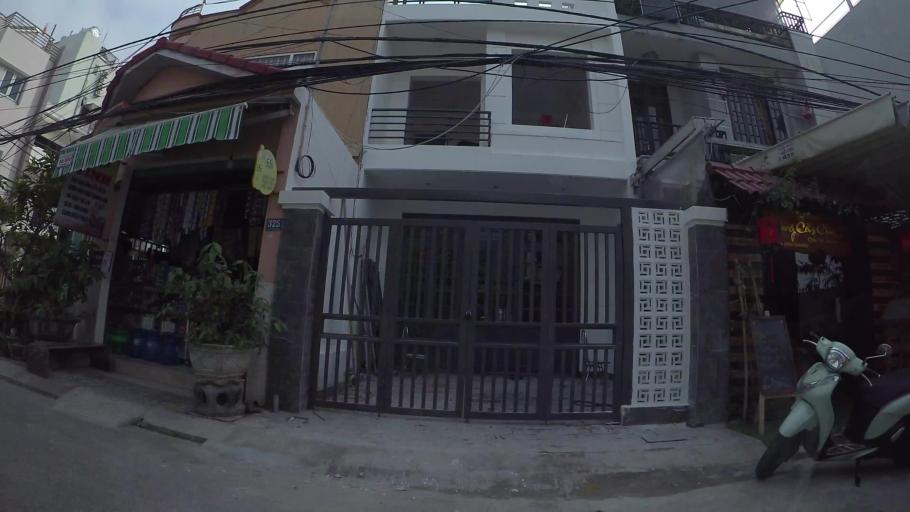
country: VN
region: Da Nang
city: Son Tra
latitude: 16.0707
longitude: 108.2331
